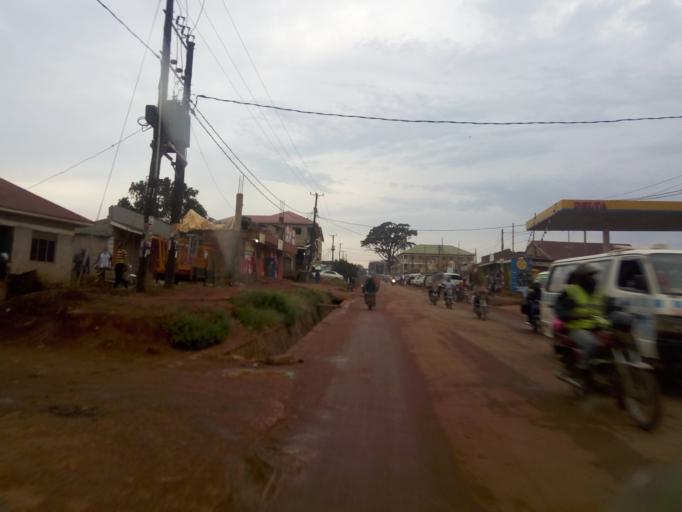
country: UG
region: Central Region
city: Kampala Central Division
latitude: 0.3251
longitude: 32.5612
